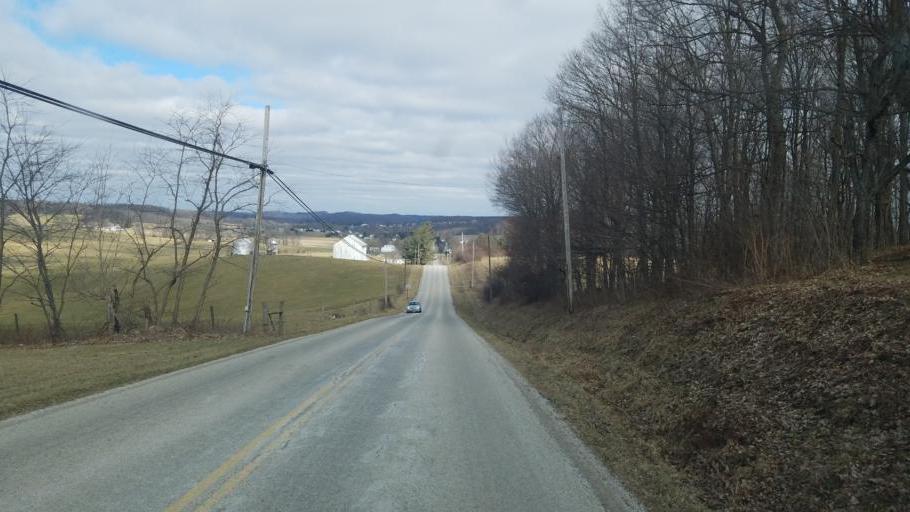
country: US
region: Ohio
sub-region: Sandusky County
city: Bellville
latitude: 40.5829
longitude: -82.5097
